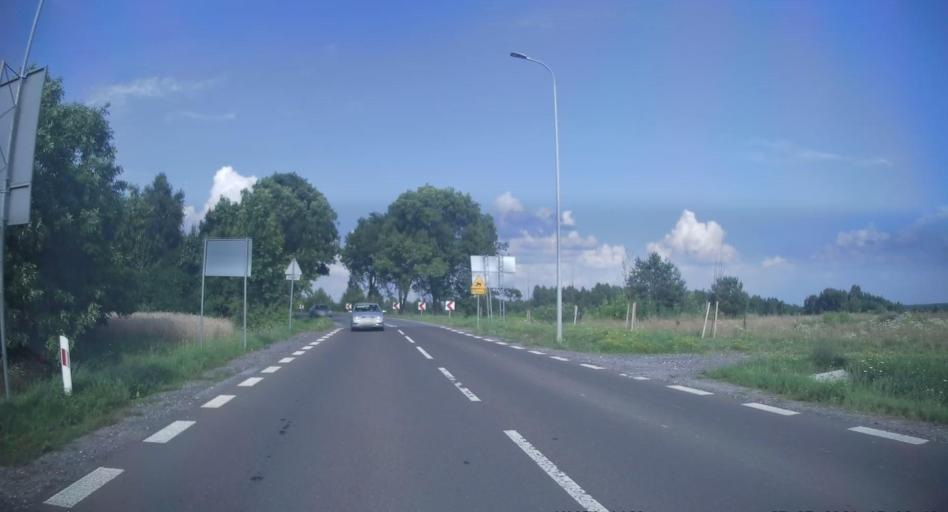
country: PL
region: Lodz Voivodeship
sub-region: Powiat tomaszowski
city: Inowlodz
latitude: 51.5318
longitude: 20.2264
